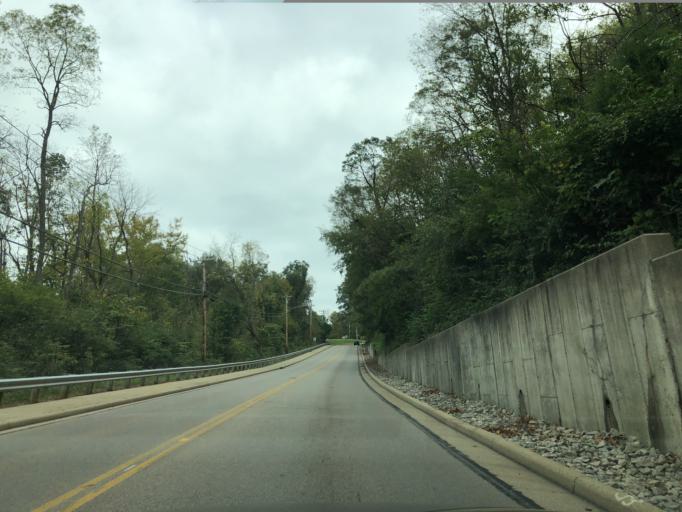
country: US
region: Ohio
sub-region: Hamilton County
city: The Village of Indian Hill
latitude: 39.2575
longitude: -84.2889
